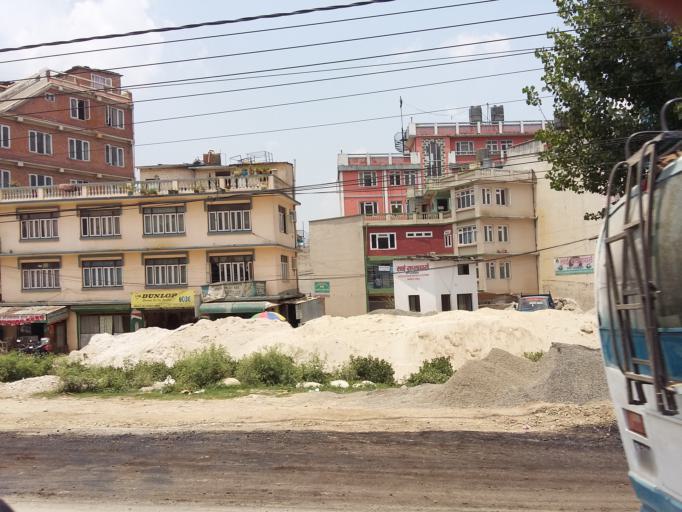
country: NP
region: Central Region
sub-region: Bagmati Zone
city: Kathmandu
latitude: 27.7366
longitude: 85.3225
